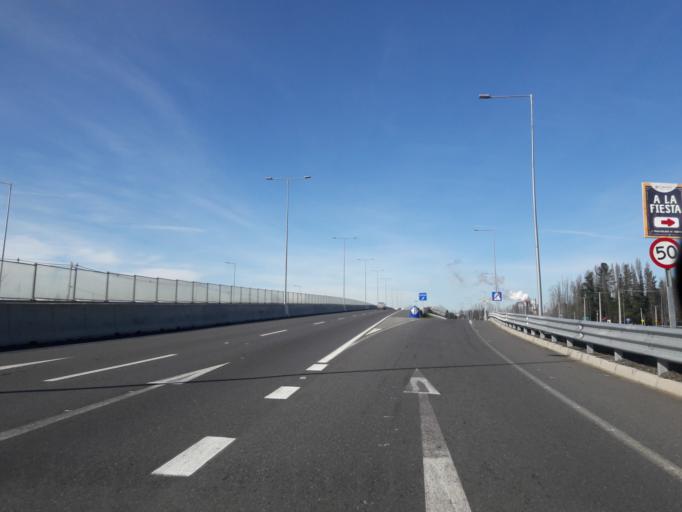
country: CL
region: Biobio
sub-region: Provincia de Biobio
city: Cabrero
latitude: -37.0381
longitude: -72.4083
